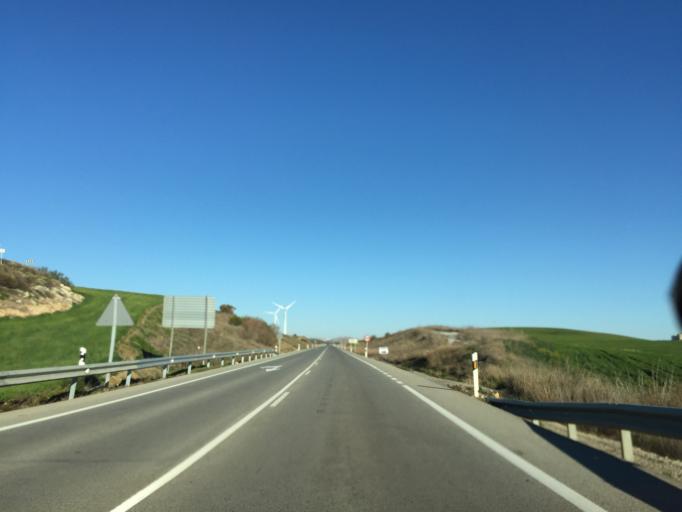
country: ES
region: Andalusia
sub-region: Provincia de Malaga
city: Ardales
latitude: 36.9231
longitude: -4.8460
